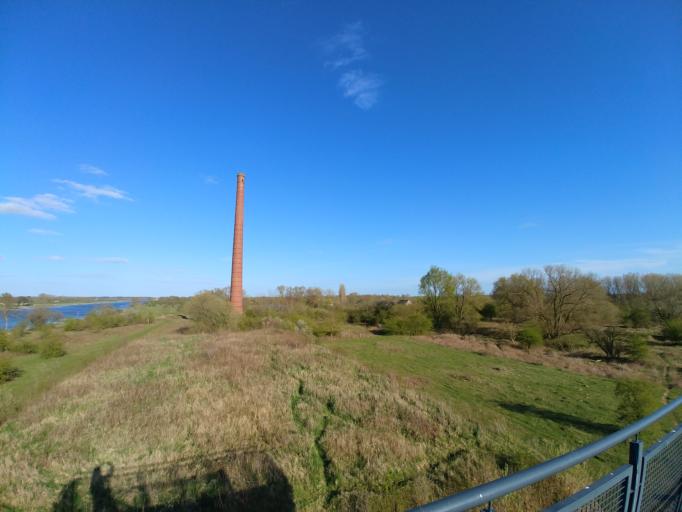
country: NL
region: Overijssel
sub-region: Gemeente Olst-Wijhe
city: Olst
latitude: 52.3719
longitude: 6.0899
